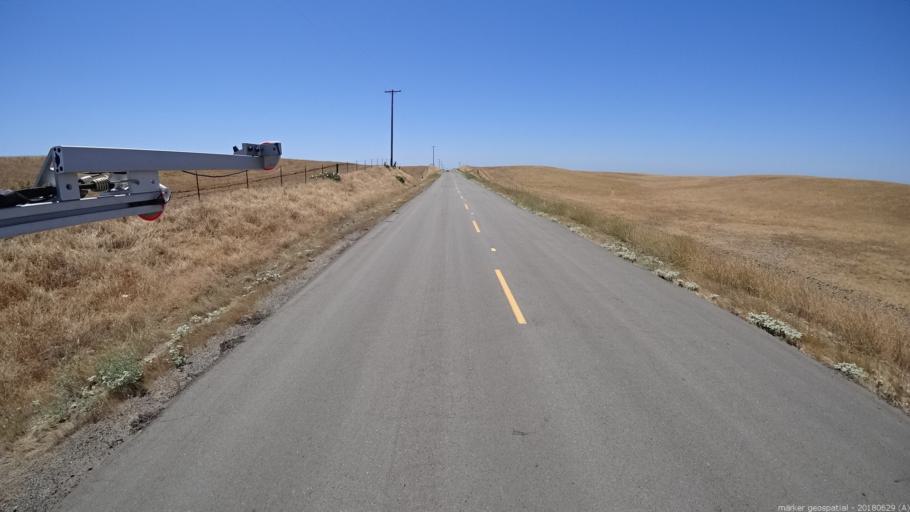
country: US
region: California
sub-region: Madera County
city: Bonadelle Ranchos-Madera Ranchos
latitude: 37.0207
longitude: -119.9471
